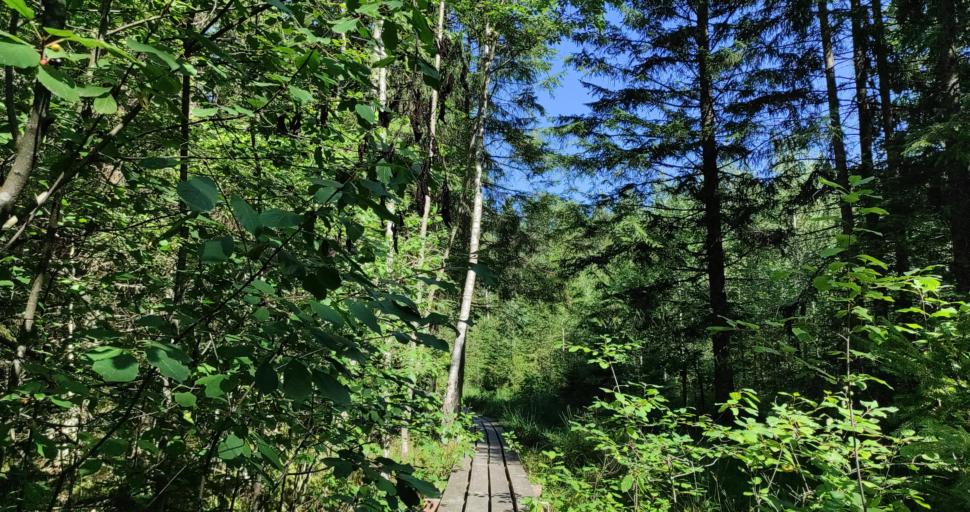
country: LT
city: Skuodas
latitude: 56.2428
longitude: 21.3984
